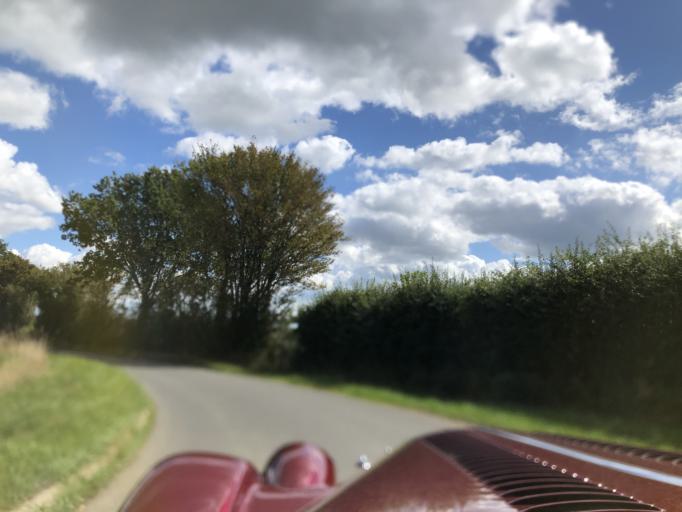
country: GB
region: England
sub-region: East Sussex
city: Northiam
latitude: 50.9944
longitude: 0.5635
